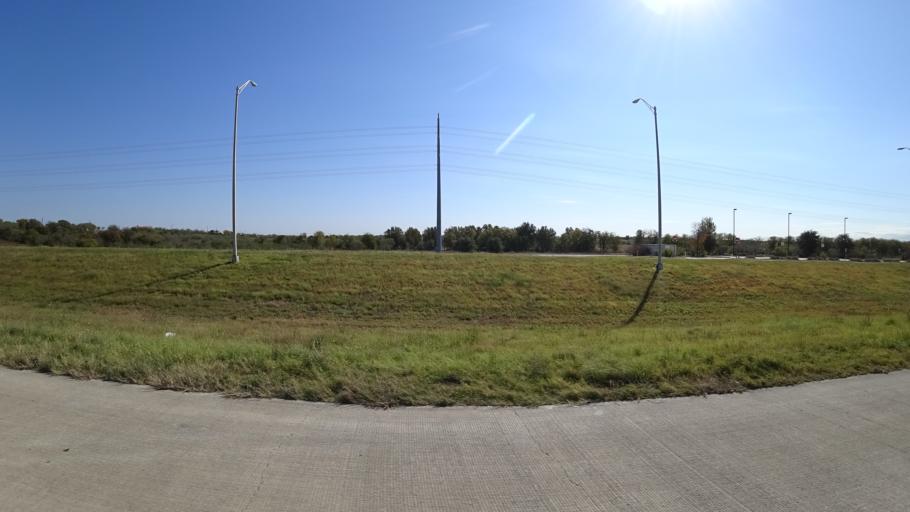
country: US
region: Texas
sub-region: Travis County
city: Garfield
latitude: 30.1706
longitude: -97.6435
